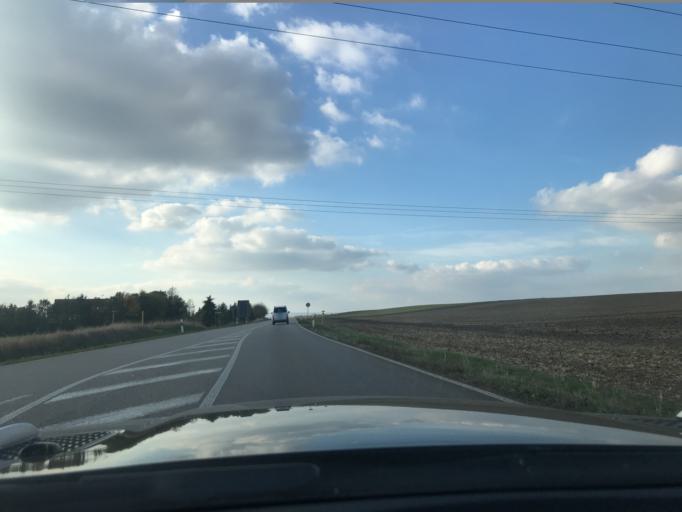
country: DE
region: Thuringia
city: Bad Langensalza
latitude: 51.1174
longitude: 10.6301
